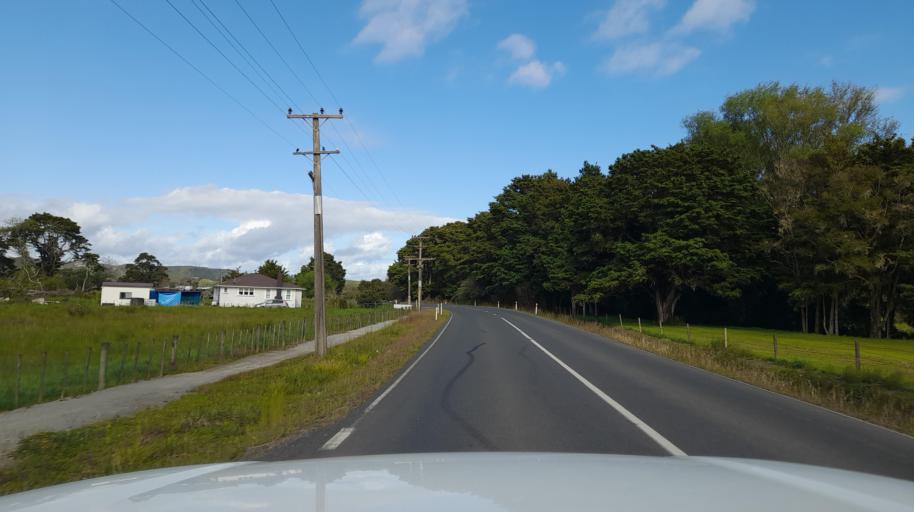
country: NZ
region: Northland
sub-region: Far North District
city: Moerewa
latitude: -35.3986
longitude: 173.9953
